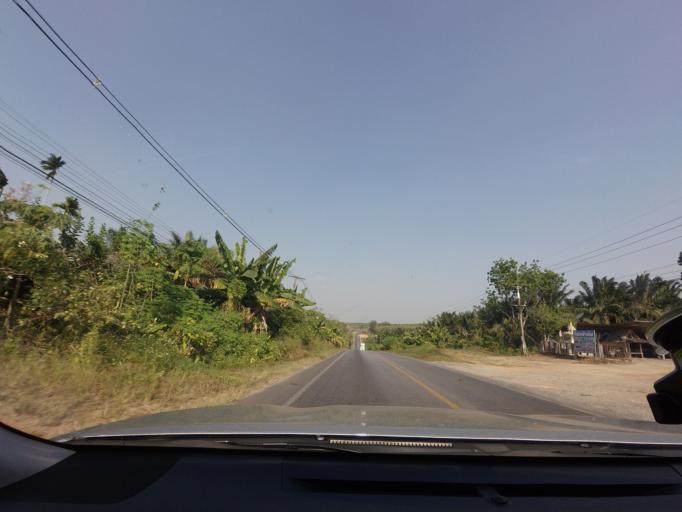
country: TH
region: Surat Thani
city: Chai Buri
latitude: 8.5702
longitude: 99.1220
